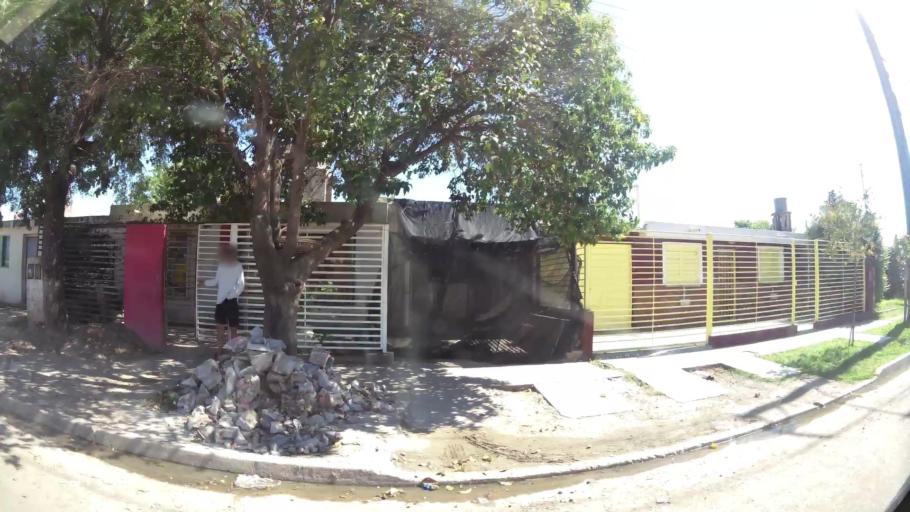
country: AR
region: Cordoba
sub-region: Departamento de Capital
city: Cordoba
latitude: -31.4430
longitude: -64.1315
